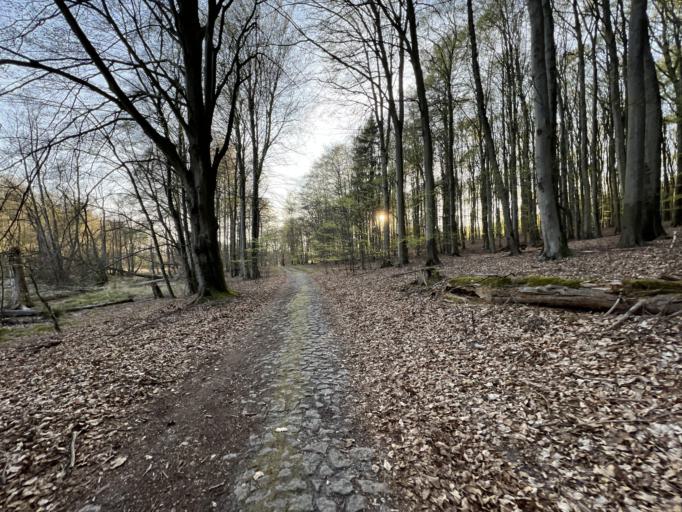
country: DE
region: Mecklenburg-Vorpommern
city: Sassnitz
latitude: 54.5371
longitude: 13.6571
